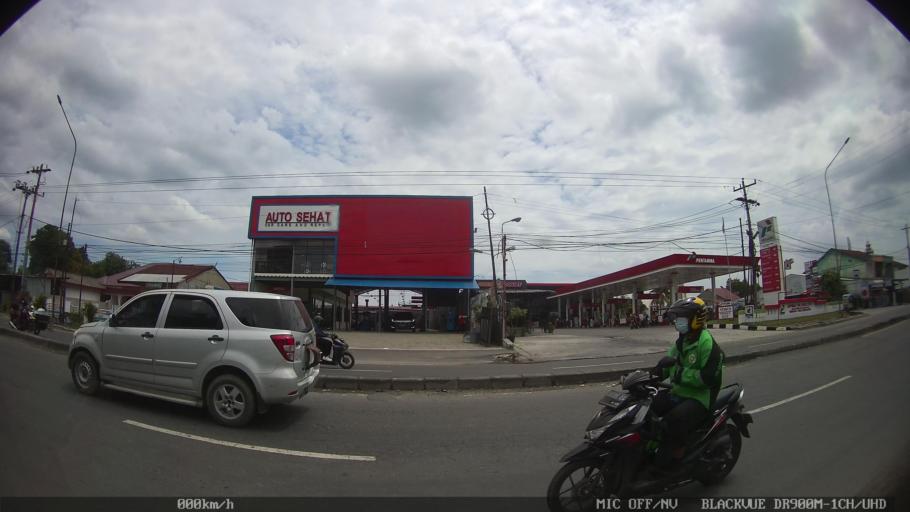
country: ID
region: North Sumatra
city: Sunggal
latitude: 3.5994
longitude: 98.5946
